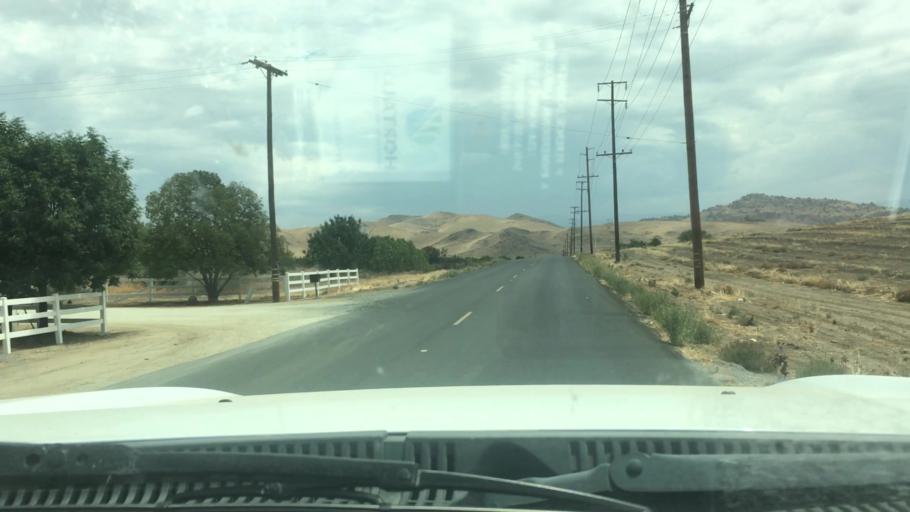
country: US
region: California
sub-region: Tulare County
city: Porterville
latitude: 36.0964
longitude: -119.0292
